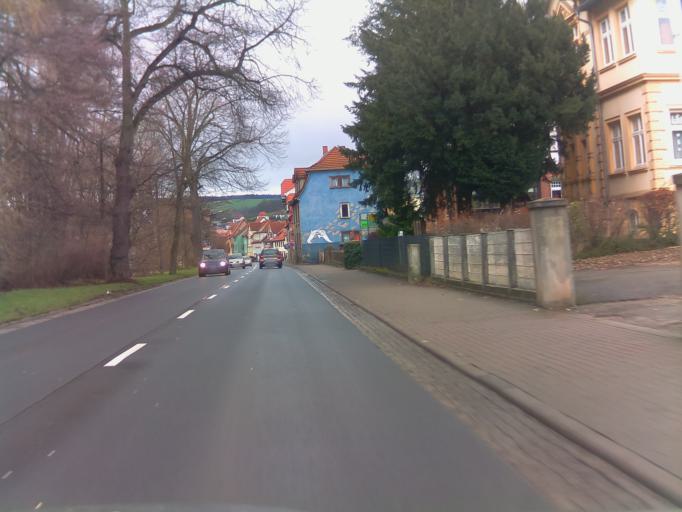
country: DE
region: Thuringia
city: Schmalkalden
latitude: 50.7195
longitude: 10.4602
